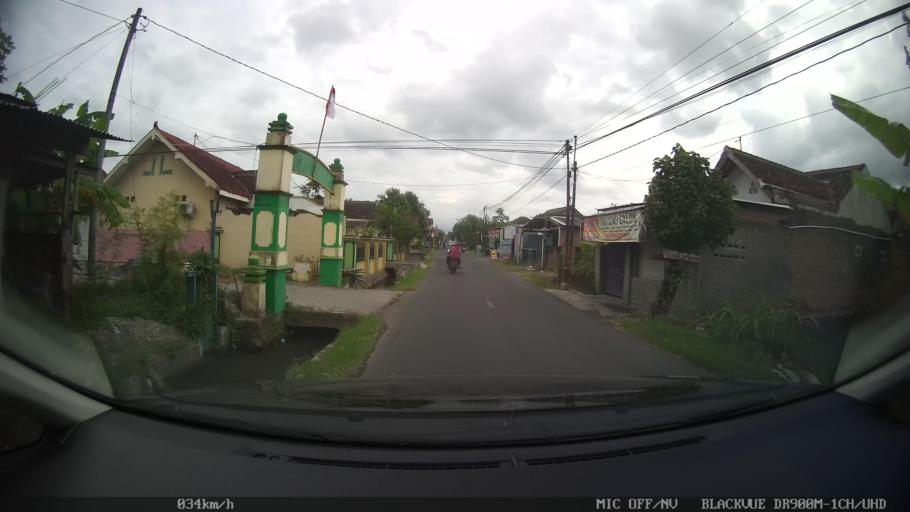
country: ID
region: Daerah Istimewa Yogyakarta
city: Depok
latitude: -7.8318
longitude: 110.4228
